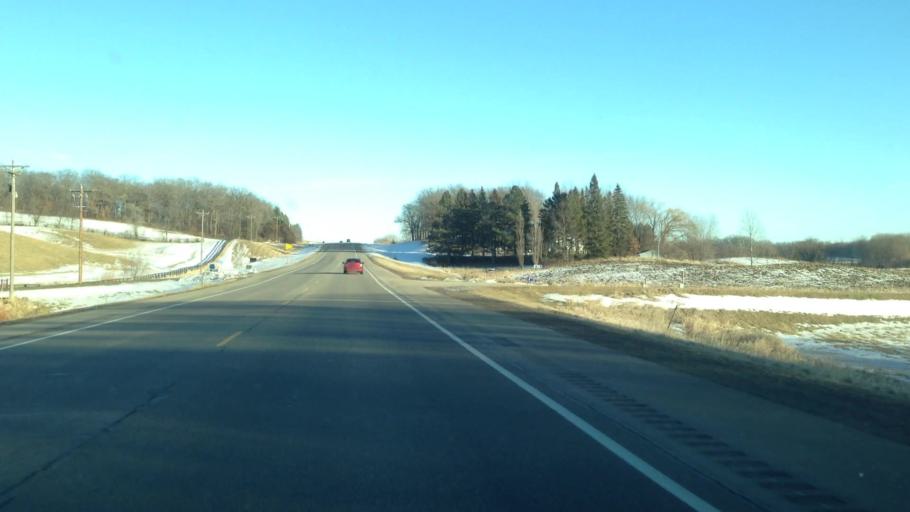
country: US
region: Minnesota
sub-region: Rice County
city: Lonsdale
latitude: 44.4791
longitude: -93.3674
